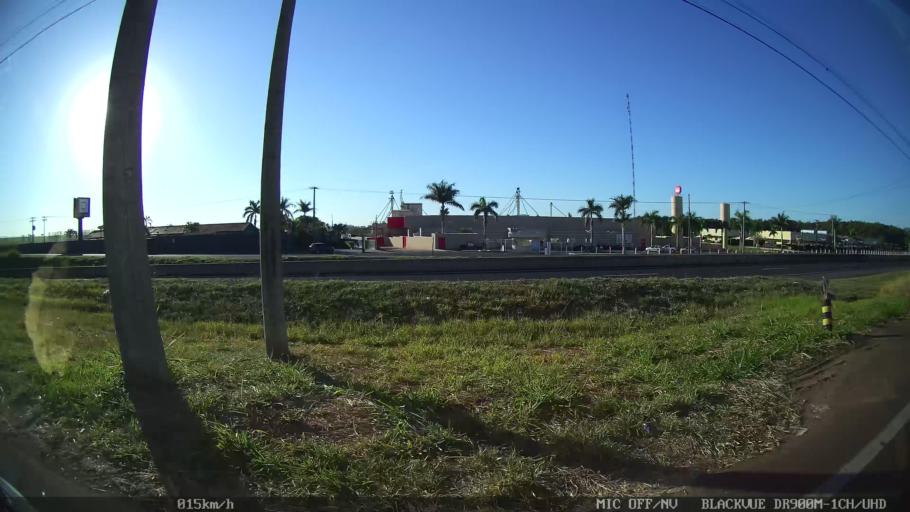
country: BR
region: Sao Paulo
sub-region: Guapiacu
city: Guapiacu
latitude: -20.7818
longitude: -49.2598
